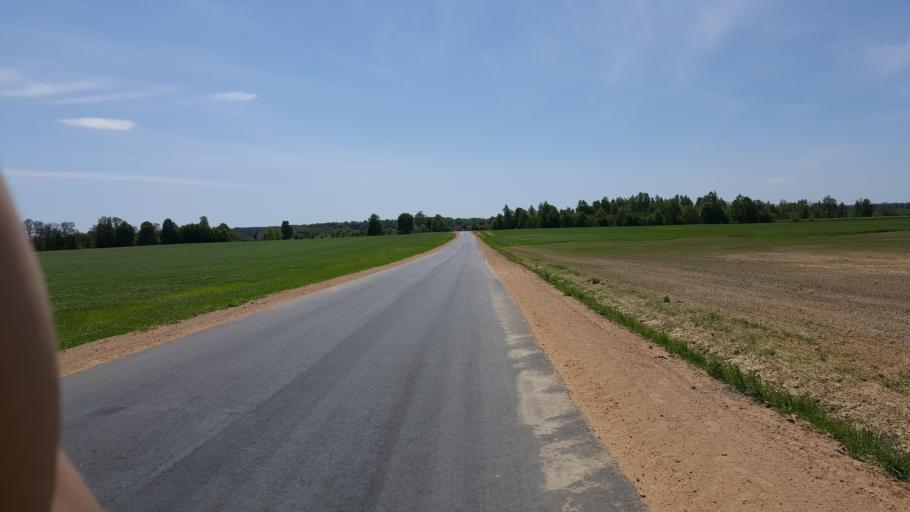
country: BY
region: Brest
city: Kobryn
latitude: 52.3512
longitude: 24.2021
